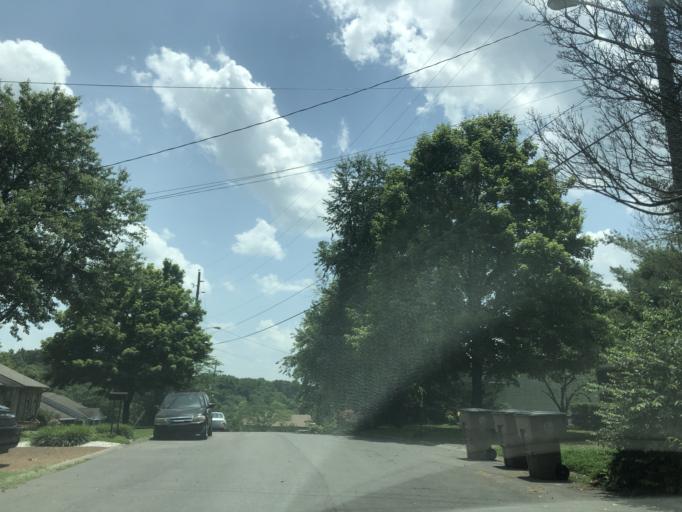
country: US
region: Tennessee
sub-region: Williamson County
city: Brentwood Estates
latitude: 36.0497
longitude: -86.6893
